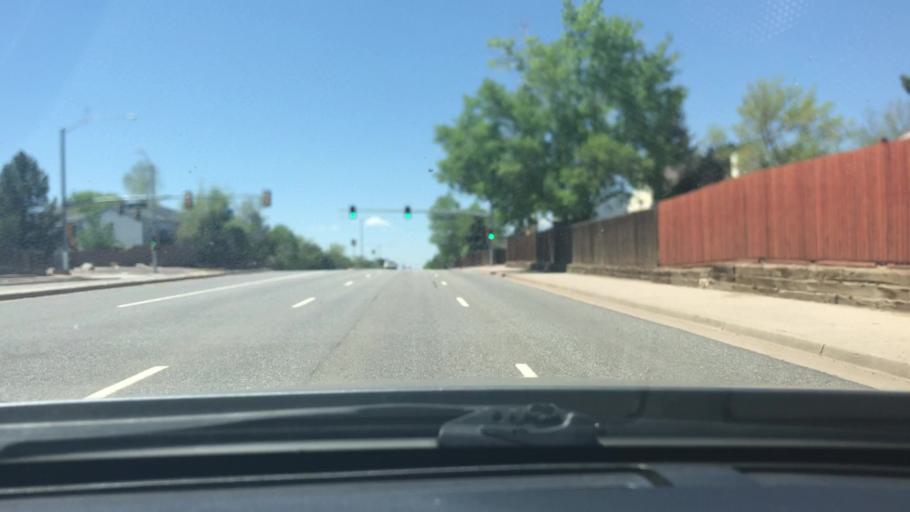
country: US
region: Colorado
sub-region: Arapahoe County
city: Dove Valley
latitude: 39.6531
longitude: -104.7548
